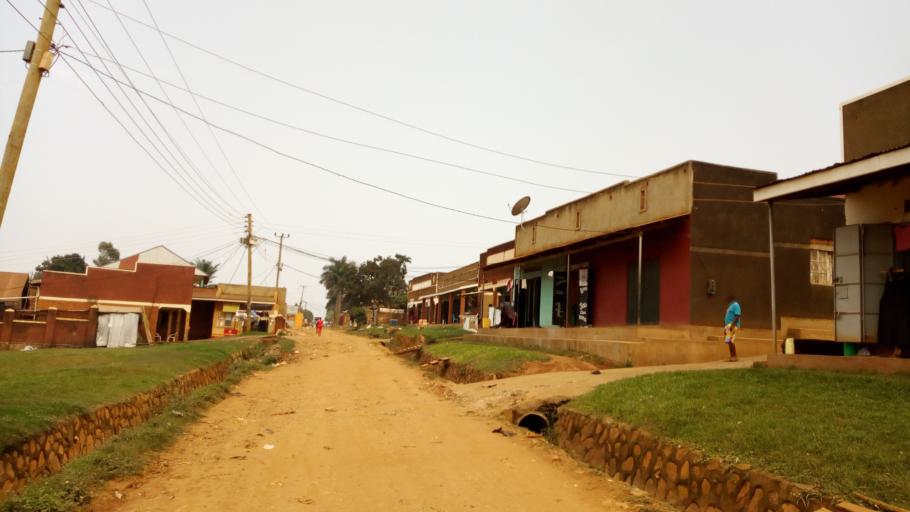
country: UG
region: Central Region
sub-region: Wakiso District
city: Kireka
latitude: 0.3195
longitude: 32.6462
